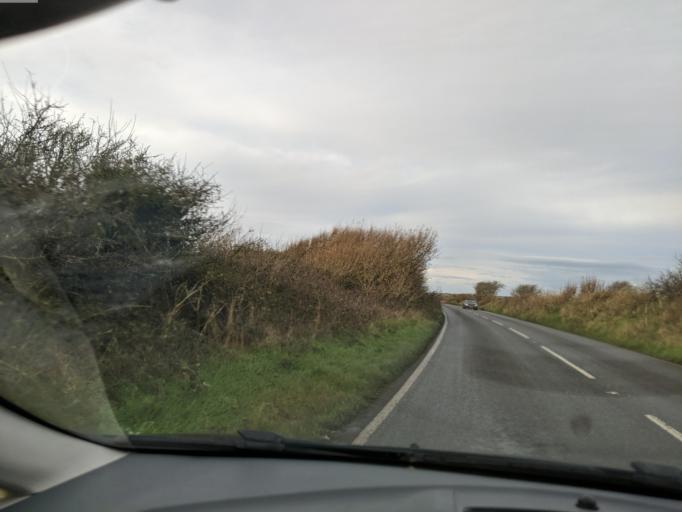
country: GB
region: England
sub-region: Cornwall
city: Jacobstow
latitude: 50.6882
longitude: -4.6152
